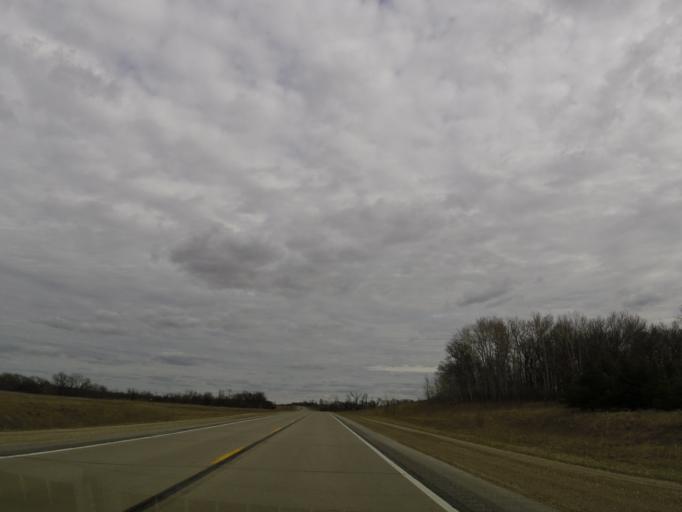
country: US
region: Minnesota
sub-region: Fillmore County
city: Spring Valley
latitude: 43.4786
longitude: -92.3416
